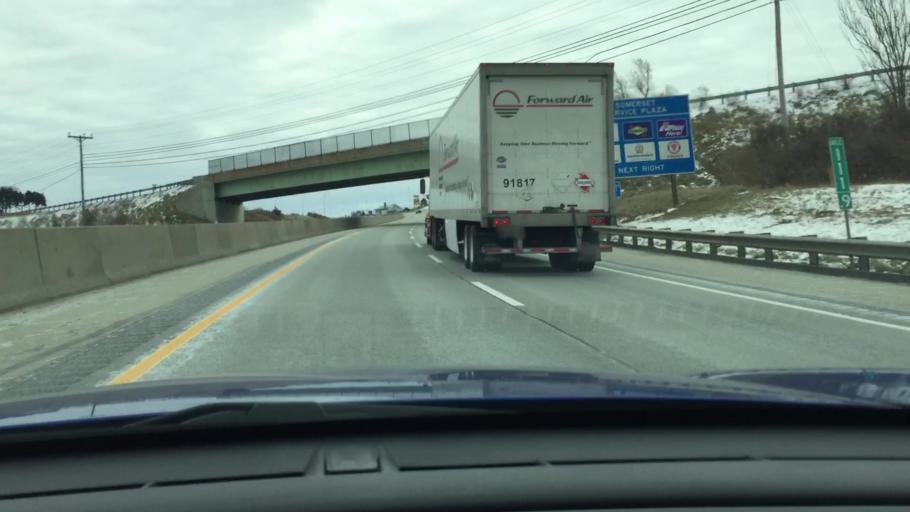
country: US
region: Pennsylvania
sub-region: Somerset County
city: Somerset
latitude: 40.0040
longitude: -79.0519
